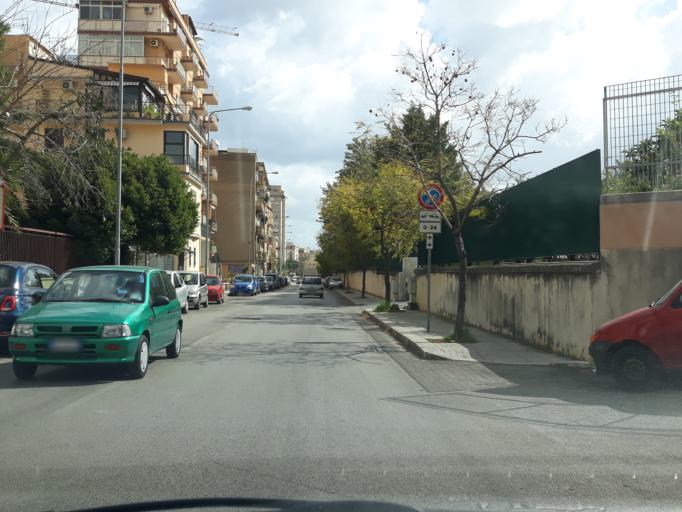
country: IT
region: Sicily
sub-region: Palermo
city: Palermo
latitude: 38.1229
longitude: 13.3238
